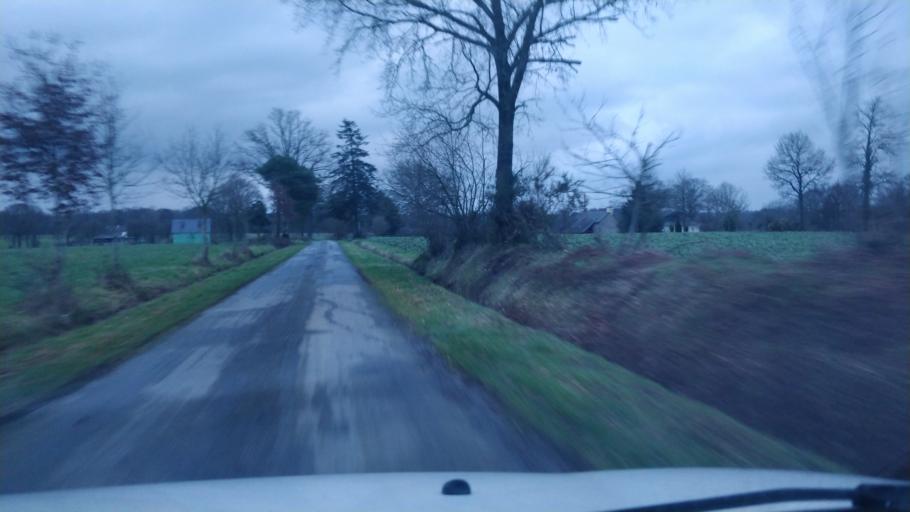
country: FR
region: Brittany
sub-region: Departement d'Ille-et-Vilaine
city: Livre-sur-Changeon
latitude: 48.1893
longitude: -1.3141
